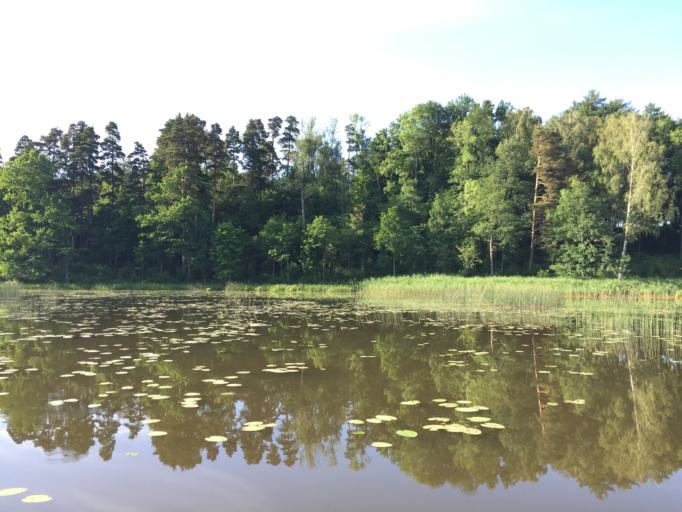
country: LV
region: Aizpute
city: Aizpute
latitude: 56.7259
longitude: 21.7397
